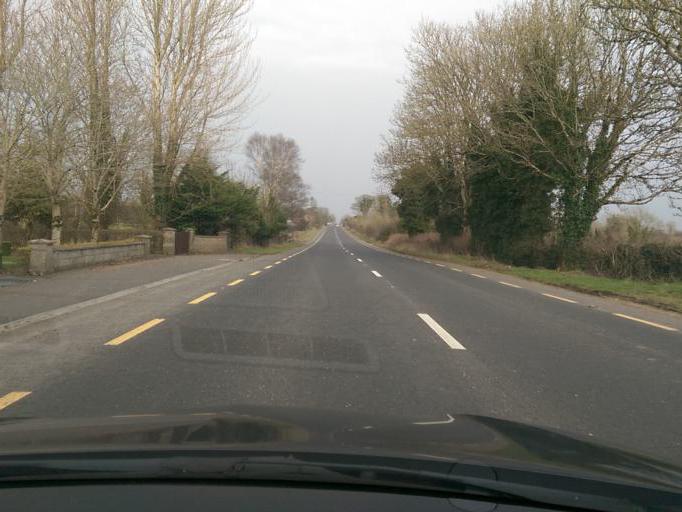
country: IE
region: Connaught
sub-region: Roscommon
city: Roscommon
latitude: 53.6434
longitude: -8.1459
